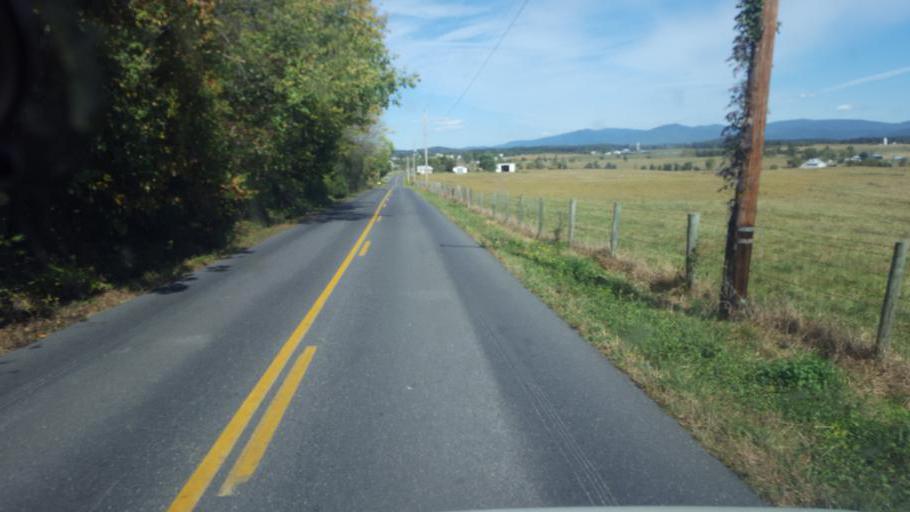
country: US
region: Virginia
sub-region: Page County
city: Stanley
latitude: 38.6073
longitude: -78.5437
